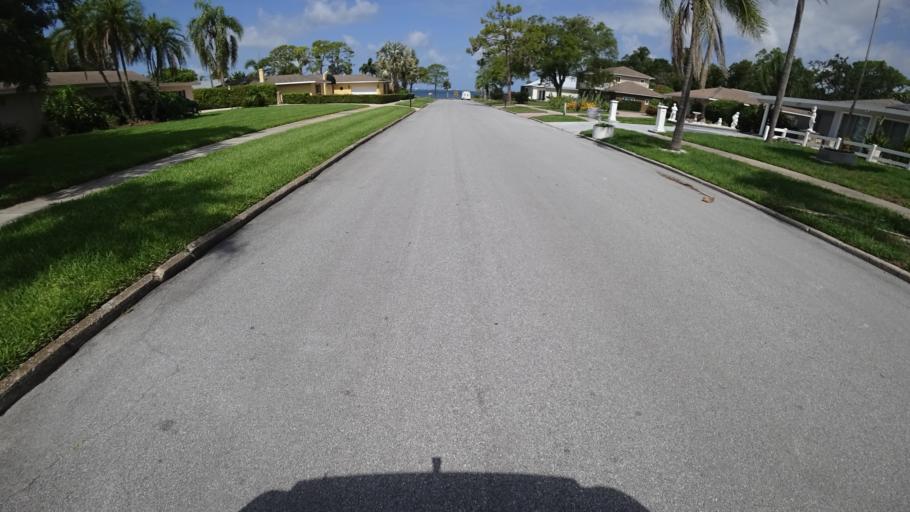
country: US
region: Florida
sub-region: Manatee County
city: Whitfield
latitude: 27.3989
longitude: -82.5683
